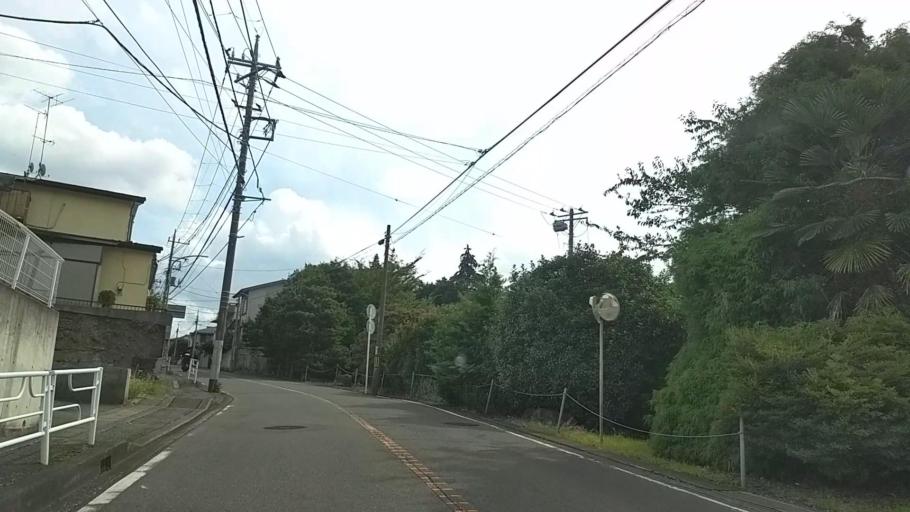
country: JP
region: Kanagawa
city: Yokohama
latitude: 35.4995
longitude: 139.5826
